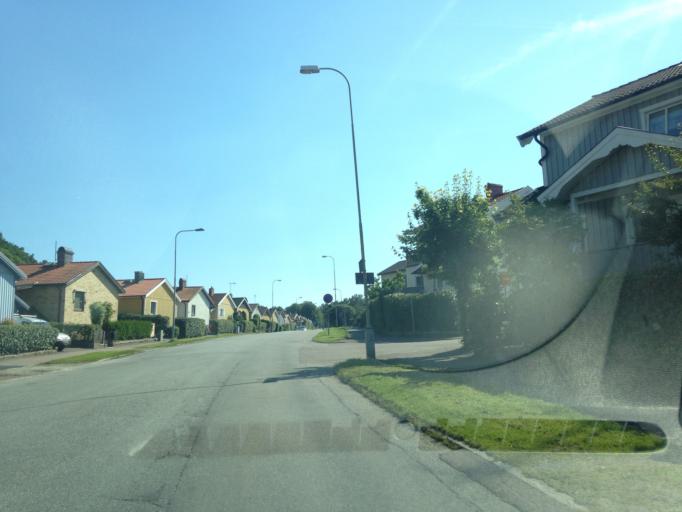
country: SE
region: Vaestra Goetaland
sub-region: Goteborg
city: Majorna
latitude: 57.7282
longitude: 11.9182
